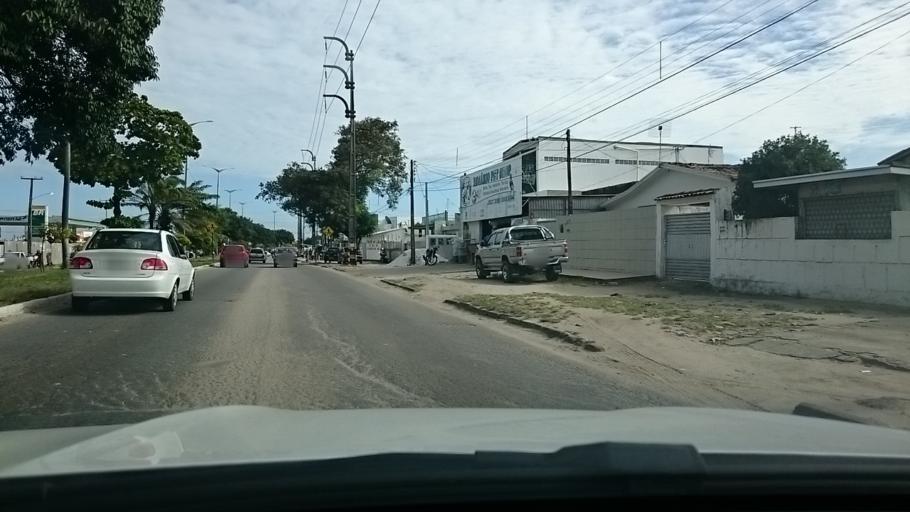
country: BR
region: Paraiba
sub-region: Joao Pessoa
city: Joao Pessoa
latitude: -7.1670
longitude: -34.8531
